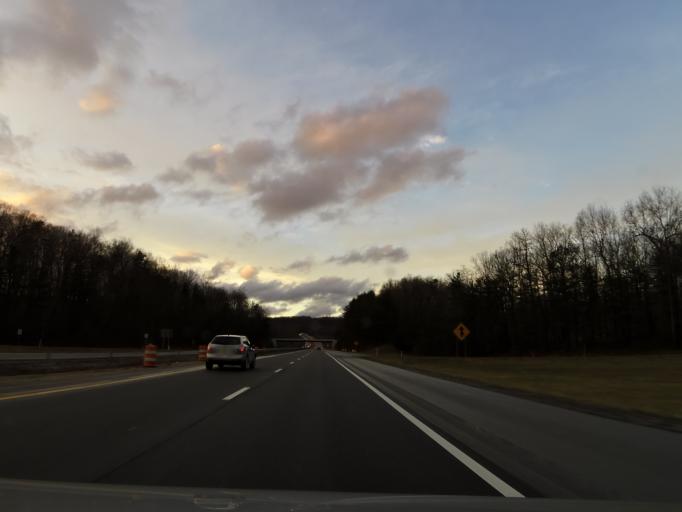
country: US
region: Tennessee
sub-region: Campbell County
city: Jacksboro
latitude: 36.4140
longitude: -84.2803
